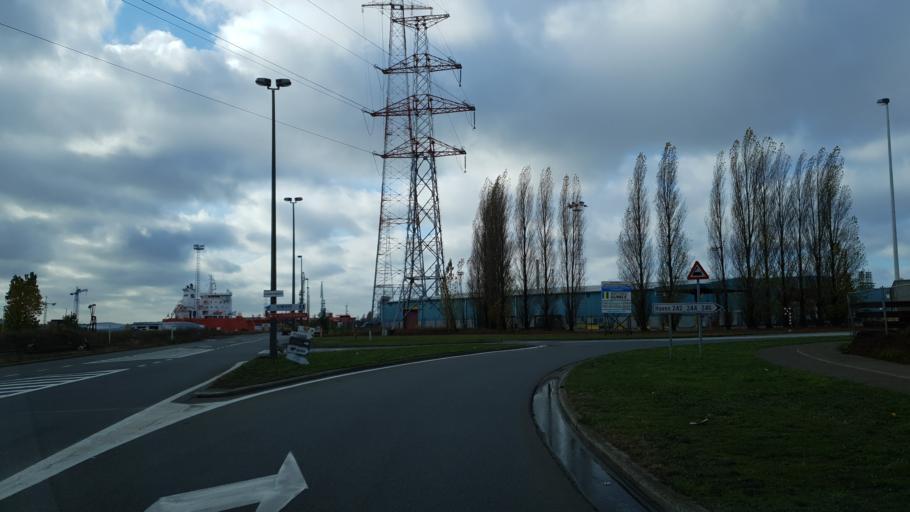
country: BE
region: Flanders
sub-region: Provincie Antwerpen
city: Zwijndrecht
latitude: 51.2643
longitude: 4.3617
